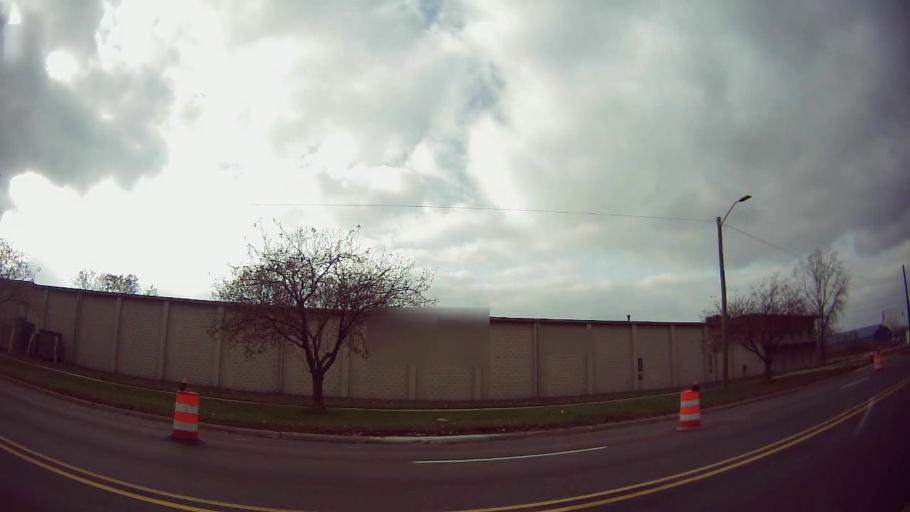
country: US
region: Michigan
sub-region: Macomb County
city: Eastpointe
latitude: 42.4731
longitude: -82.9865
